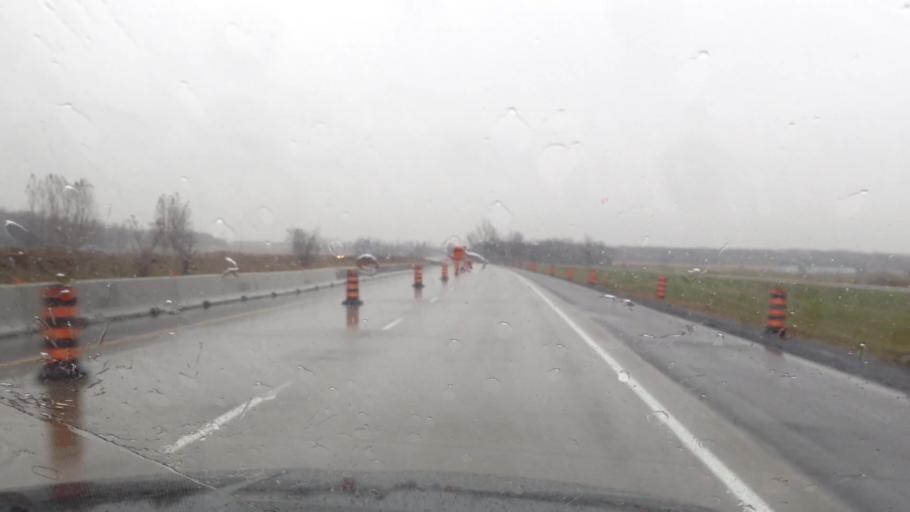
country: CA
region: Ontario
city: Hawkesbury
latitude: 45.4712
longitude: -74.6716
